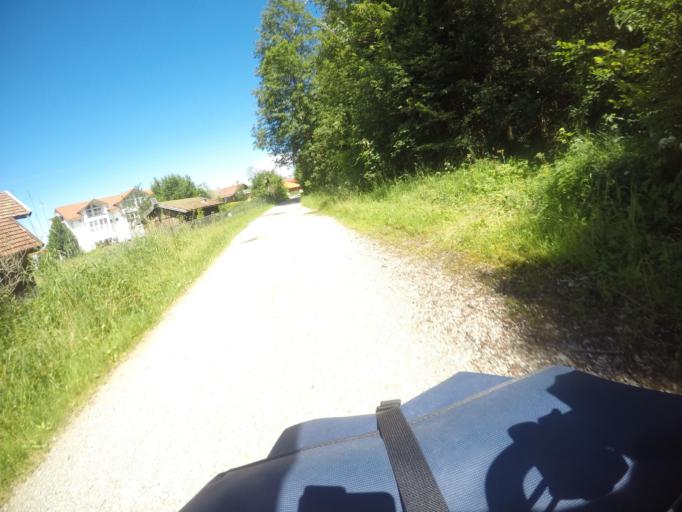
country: AT
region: Tyrol
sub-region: Politischer Bezirk Reutte
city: Musau
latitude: 47.5677
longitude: 10.6670
